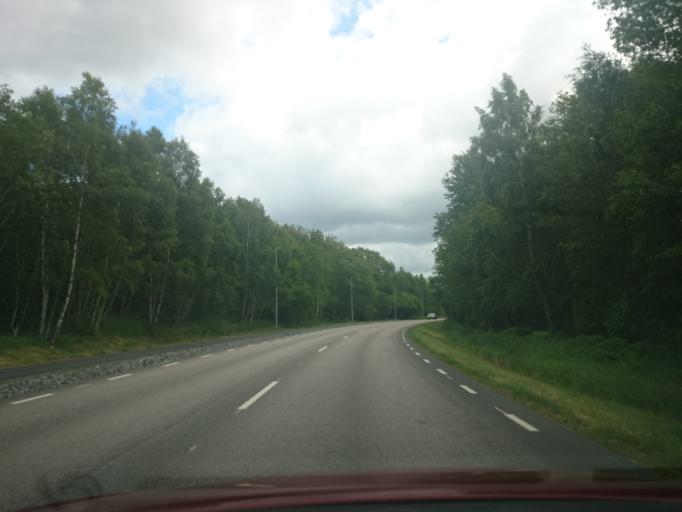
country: SE
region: Vaestra Goetaland
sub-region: Harryda Kommun
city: Molnlycke
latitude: 57.6718
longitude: 12.0868
